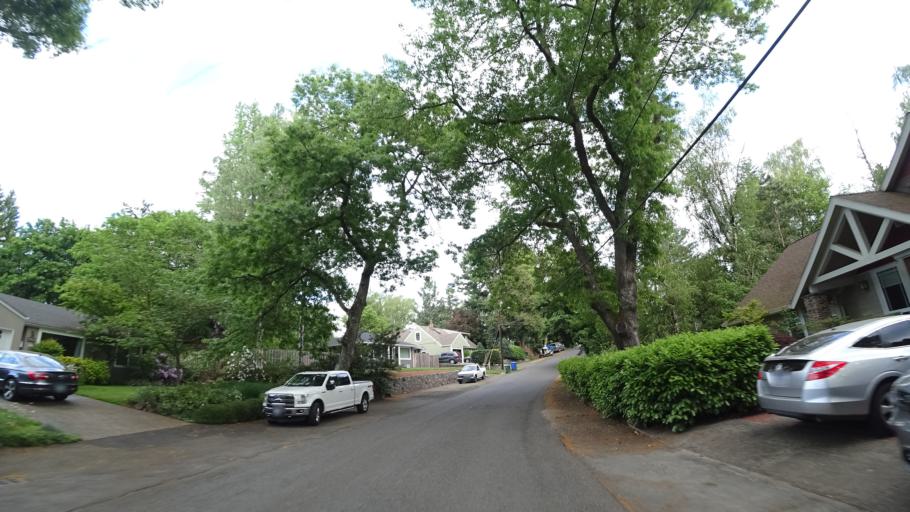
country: US
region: Oregon
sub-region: Washington County
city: Garden Home-Whitford
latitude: 45.4780
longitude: -122.7297
